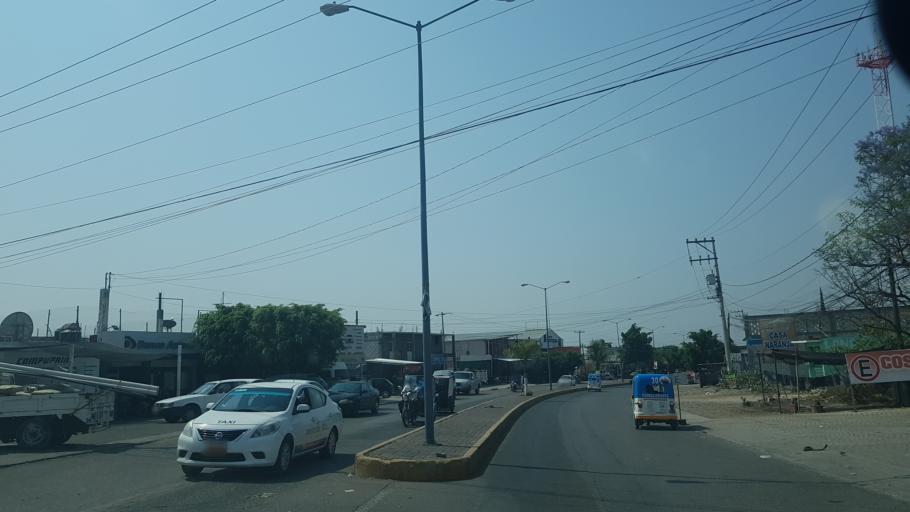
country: MX
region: Morelos
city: Amayuca
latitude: 18.7213
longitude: -98.7940
